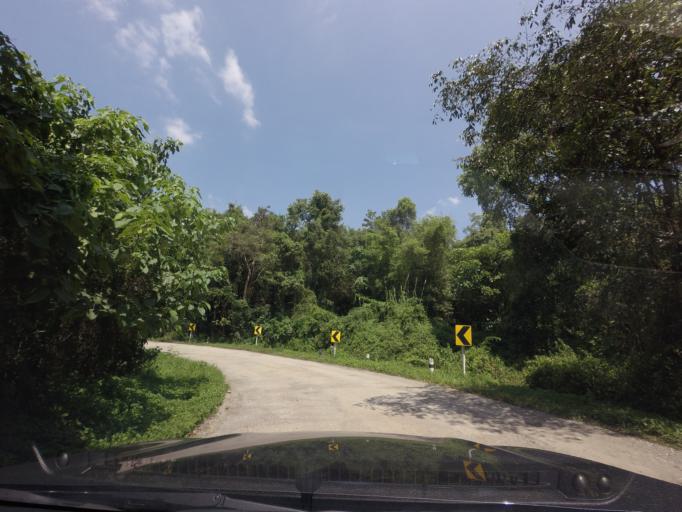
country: TH
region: Loei
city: Na Haeo
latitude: 17.6109
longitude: 100.8952
